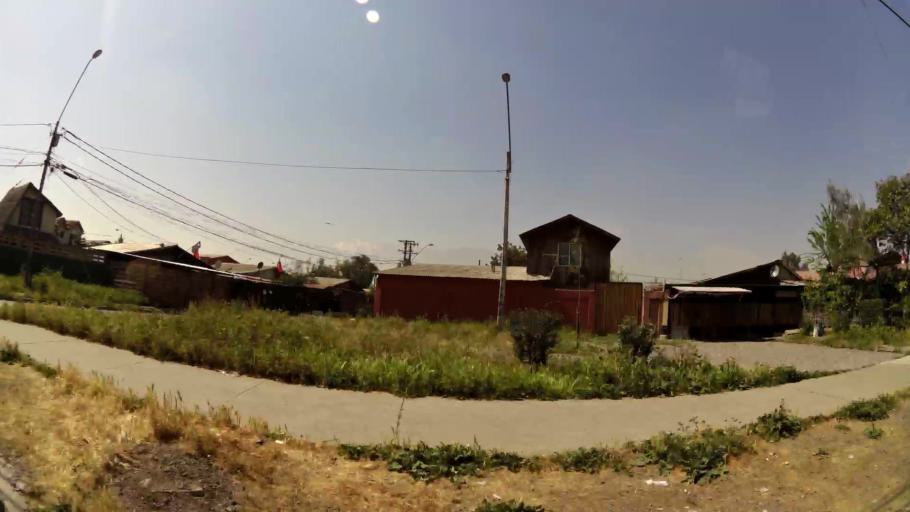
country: CL
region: Santiago Metropolitan
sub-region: Provincia de Santiago
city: La Pintana
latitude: -33.5532
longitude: -70.6129
